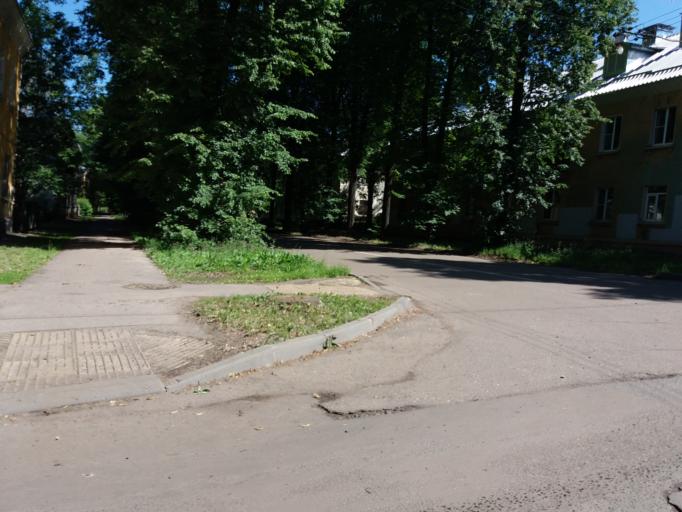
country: RU
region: Jaroslavl
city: Yaroslavl
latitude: 57.6406
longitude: 39.8348
